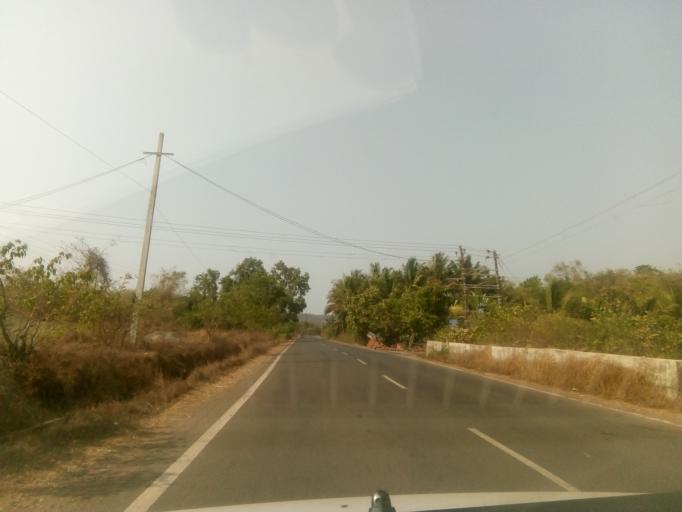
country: IN
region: Goa
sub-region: North Goa
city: Pernem
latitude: 15.6893
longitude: 73.8401
